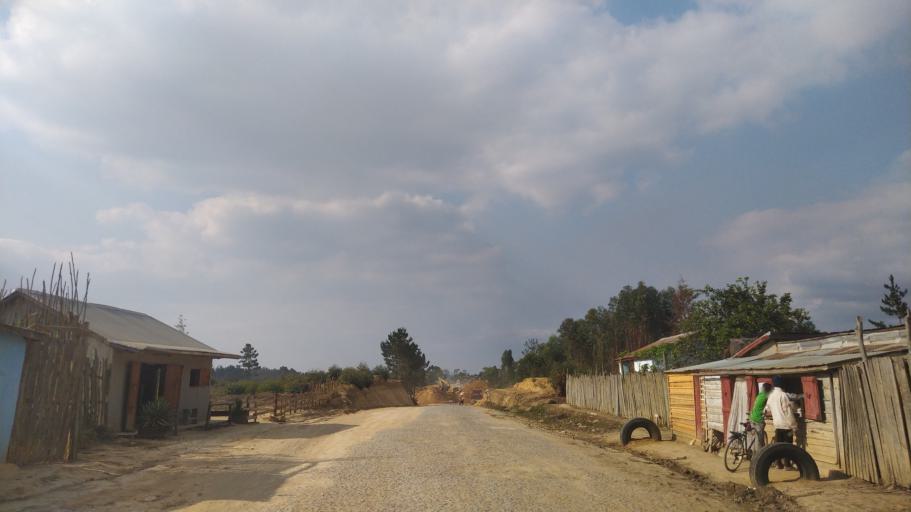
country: MG
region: Alaotra Mangoro
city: Moramanga
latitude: -18.6345
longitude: 48.2759
